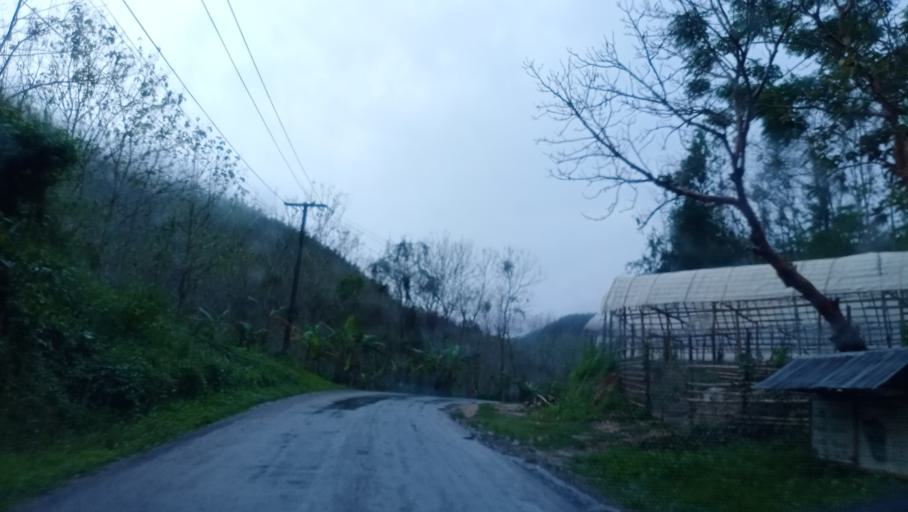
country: LA
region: Phongsali
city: Khoa
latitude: 21.0630
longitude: 102.4816
